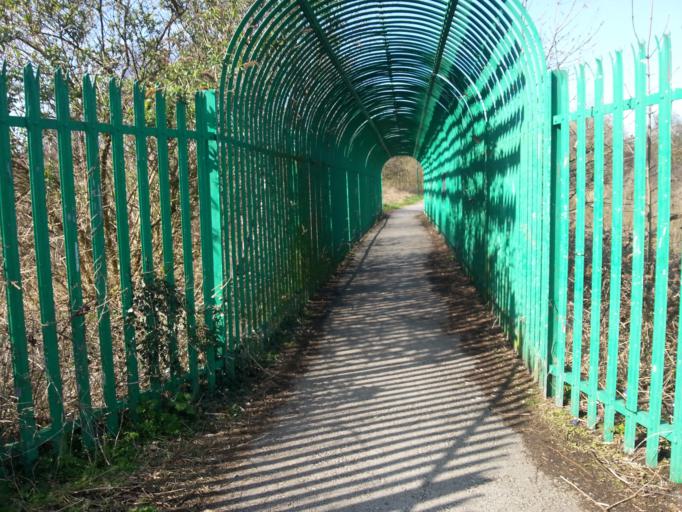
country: GB
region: England
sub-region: Knowsley
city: Huyton
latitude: 53.3619
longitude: -2.8464
